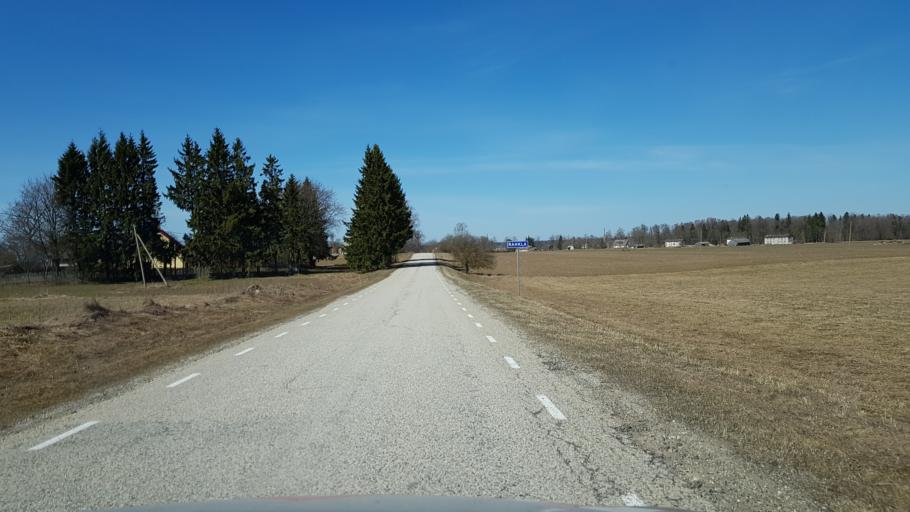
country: EE
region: Laeaene-Virumaa
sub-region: Vinni vald
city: Vinni
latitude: 59.0904
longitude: 26.5365
